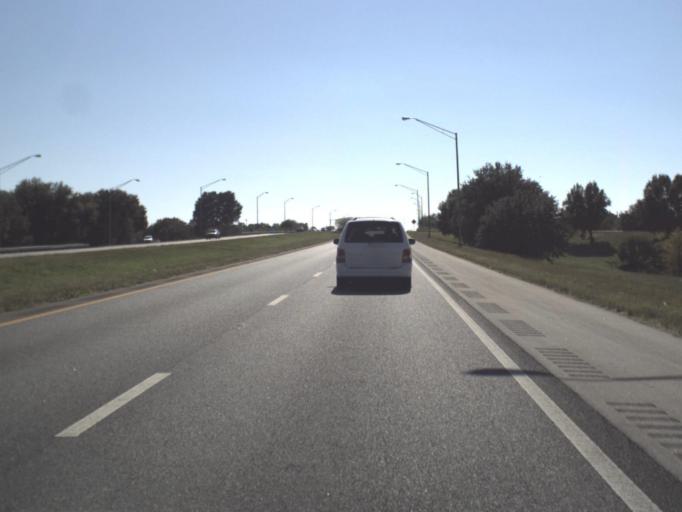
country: US
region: Florida
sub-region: Seminole County
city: Oviedo
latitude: 28.6604
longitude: -81.2306
